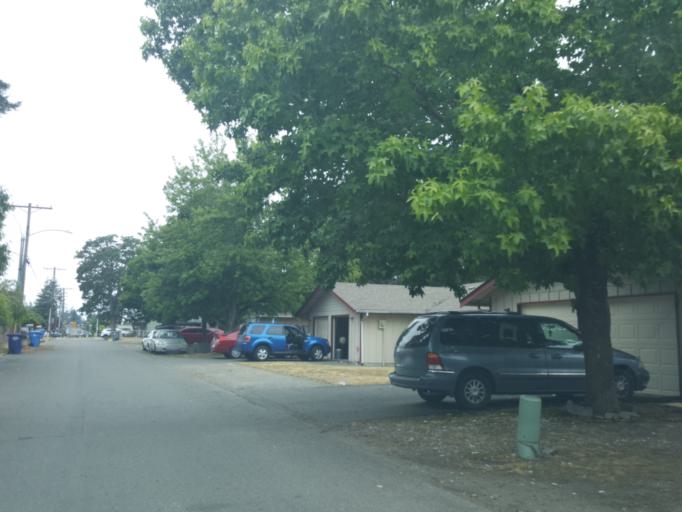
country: US
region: Washington
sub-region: Pierce County
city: Lakewood
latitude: 47.1702
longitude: -122.5136
